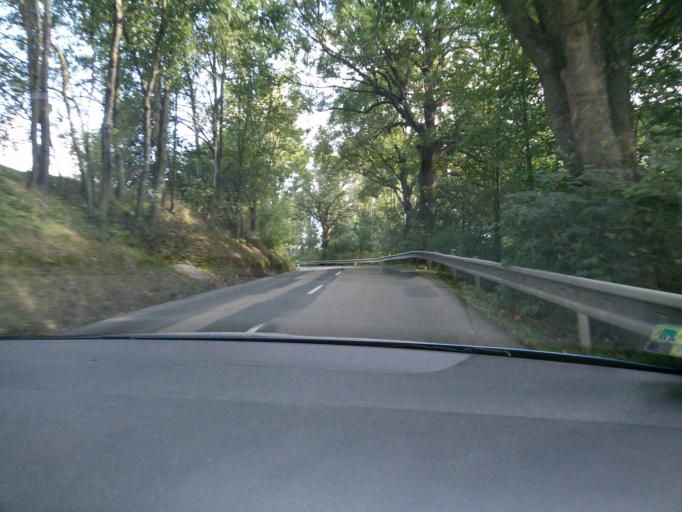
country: CZ
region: South Moravian
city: Olesnice
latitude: 49.5431
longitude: 16.4379
